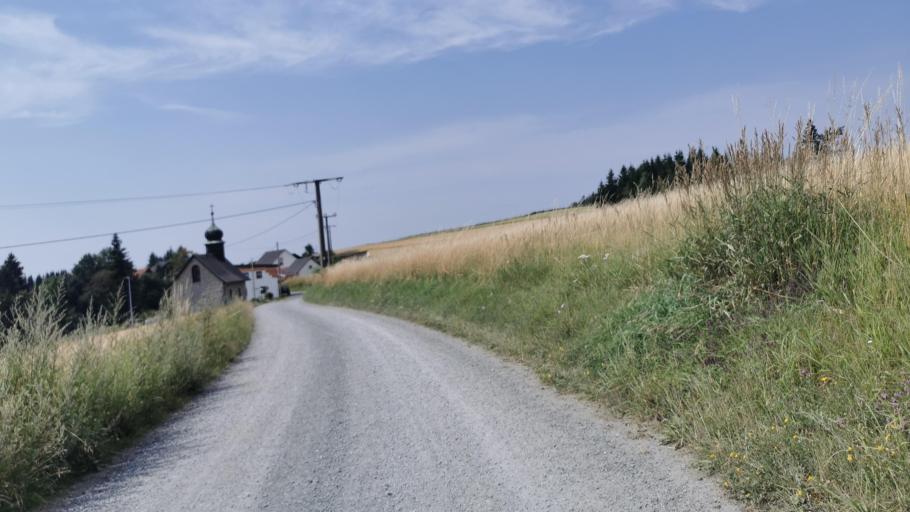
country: DE
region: Bavaria
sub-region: Upper Franconia
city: Wilhelmsthal
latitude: 50.2826
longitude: 11.3856
